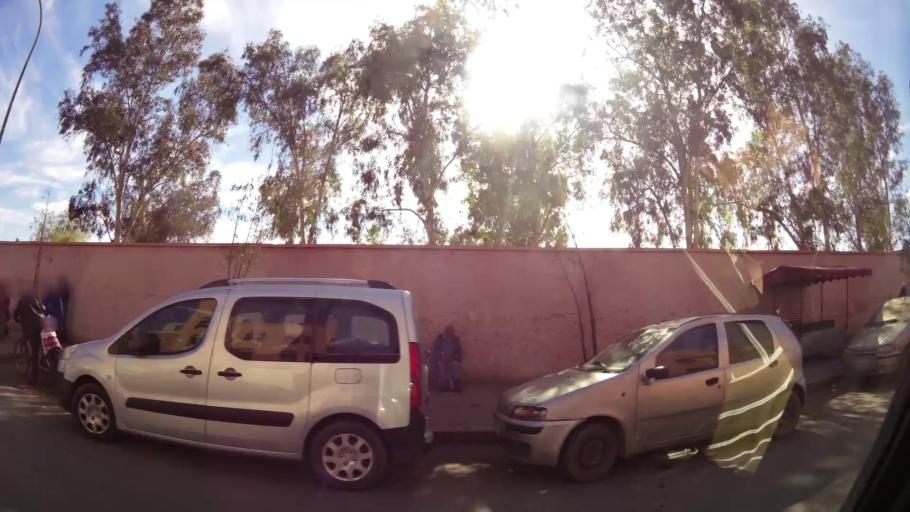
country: MA
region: Marrakech-Tensift-Al Haouz
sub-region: Marrakech
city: Marrakesh
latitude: 31.6069
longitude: -7.9638
